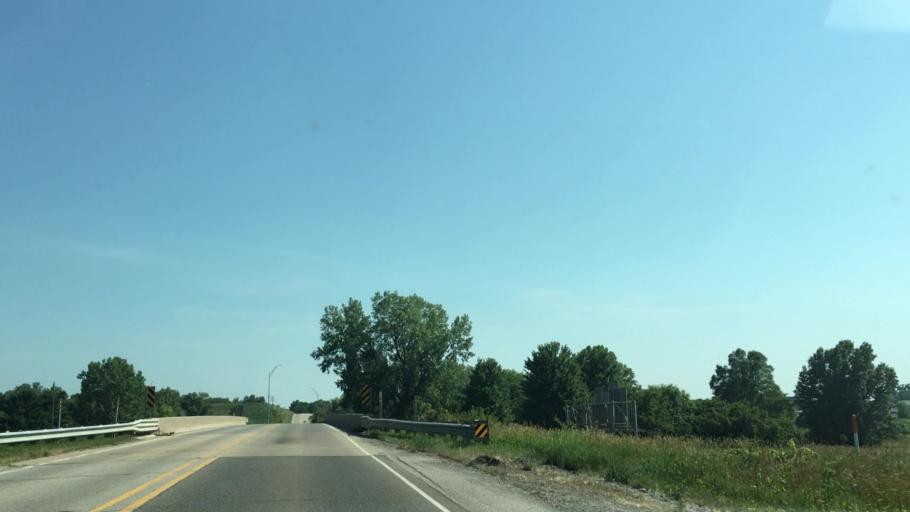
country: US
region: Iowa
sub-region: Johnson County
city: Tiffin
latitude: 41.6946
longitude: -91.6666
